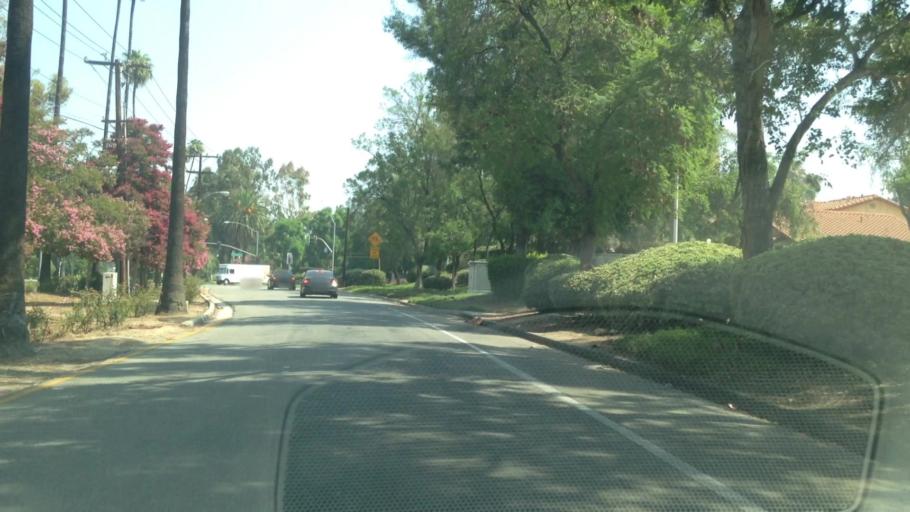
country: US
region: California
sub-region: Riverside County
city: Riverside
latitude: 33.9451
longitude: -117.3705
